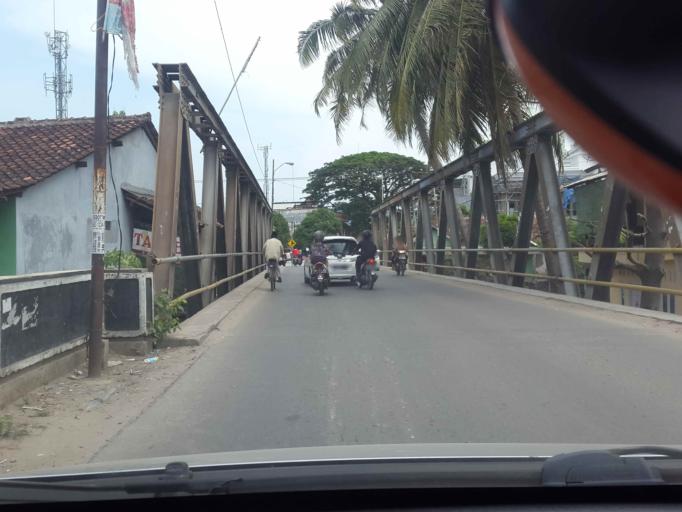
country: ID
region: Lampung
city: Bandarlampung
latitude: -5.4527
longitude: 105.2581
